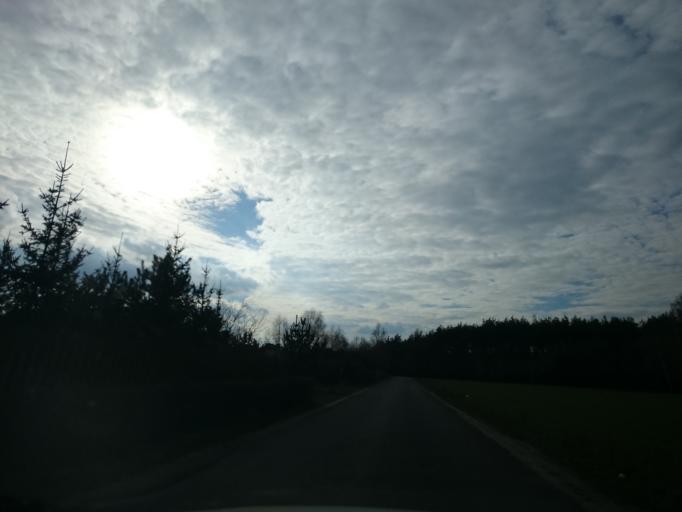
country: PL
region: Kujawsko-Pomorskie
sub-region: Powiat torunski
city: Lubicz Gorny
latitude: 53.0510
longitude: 18.8437
